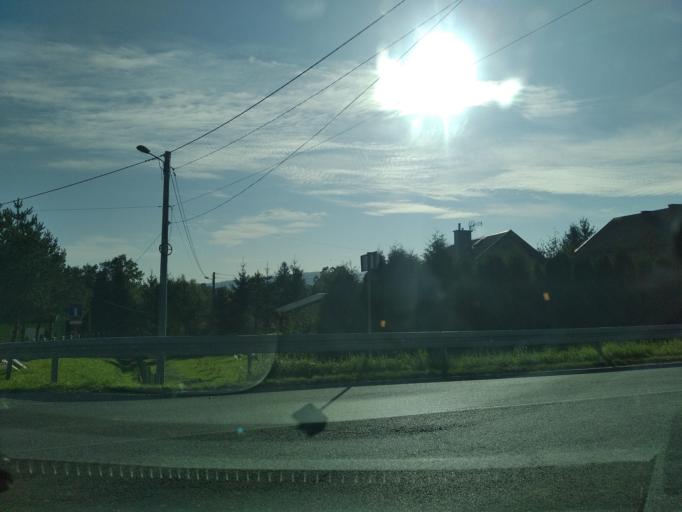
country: PL
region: Subcarpathian Voivodeship
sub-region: Powiat krosnienski
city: Sieniawa
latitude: 49.5649
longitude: 21.9374
